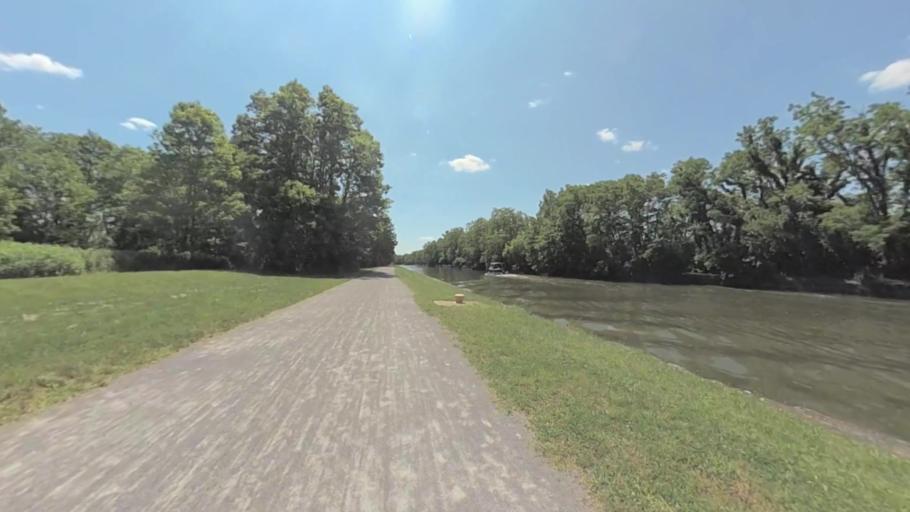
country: US
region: New York
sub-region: Monroe County
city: Pittsford
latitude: 43.0703
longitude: -77.4905
